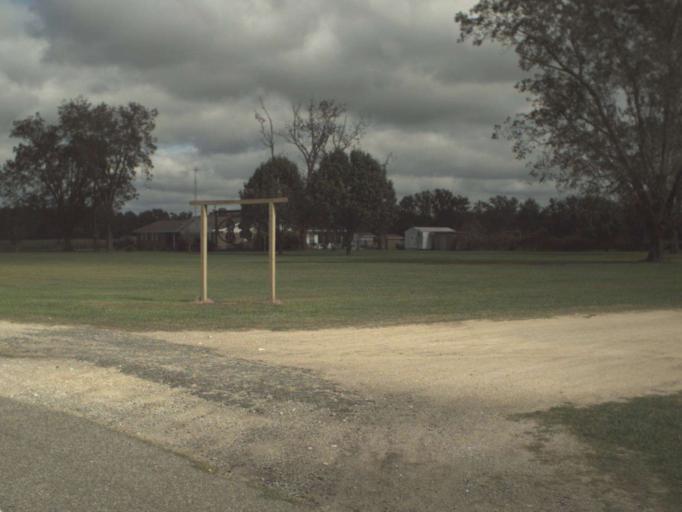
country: US
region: Florida
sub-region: Calhoun County
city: Blountstown
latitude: 30.6010
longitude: -85.1391
